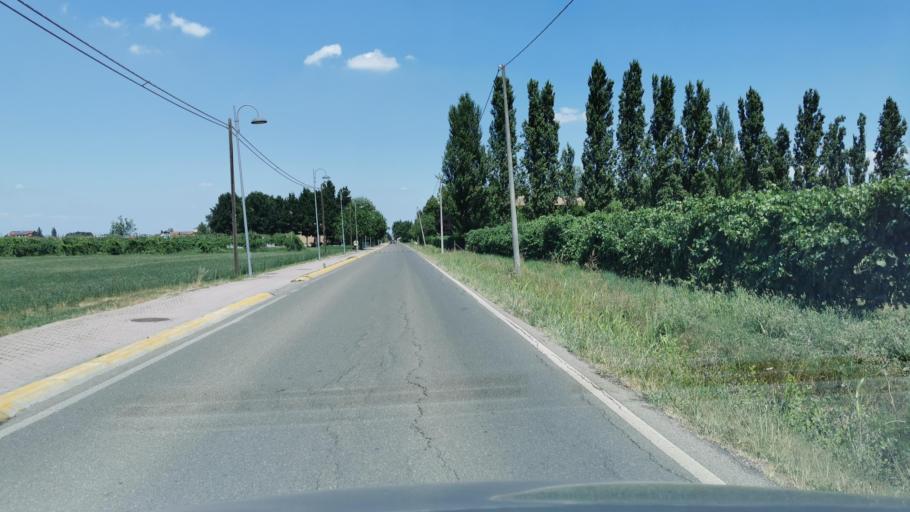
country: IT
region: Emilia-Romagna
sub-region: Provincia di Modena
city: Fossoli
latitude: 44.8107
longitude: 10.8905
